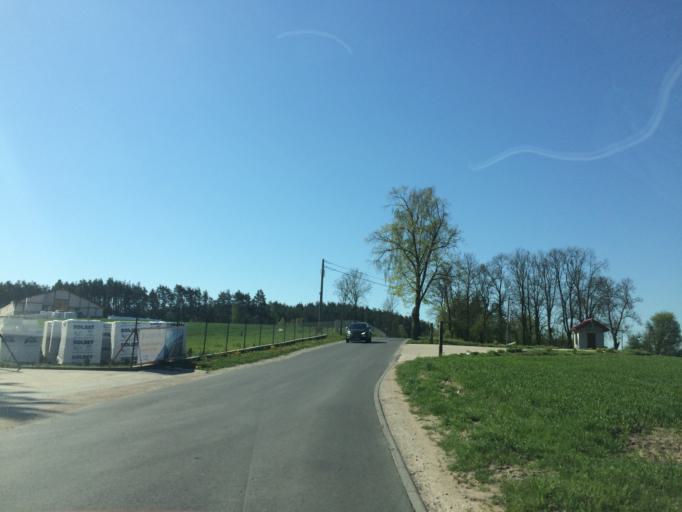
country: PL
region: Warmian-Masurian Voivodeship
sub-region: Powiat nowomiejski
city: Nowe Miasto Lubawskie
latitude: 53.4966
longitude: 19.5785
